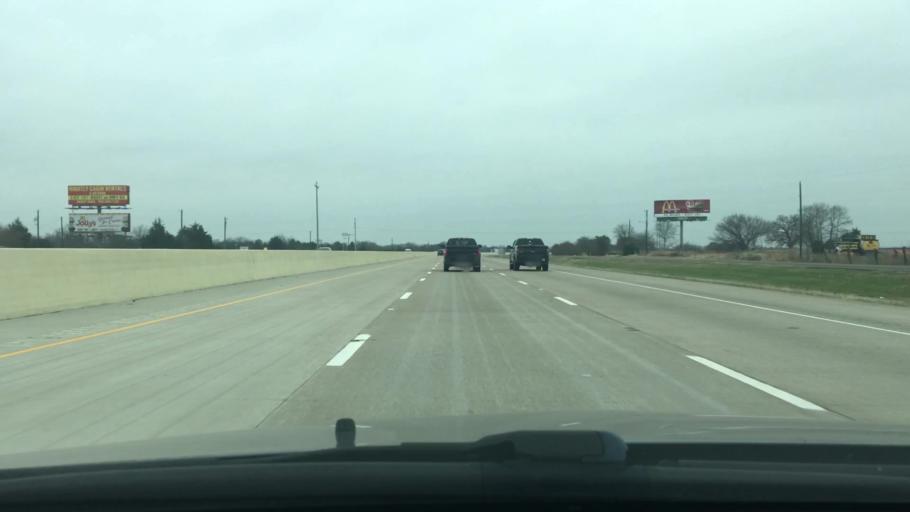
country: US
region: Texas
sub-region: Navarro County
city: Corsicana
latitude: 31.9889
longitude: -96.4258
